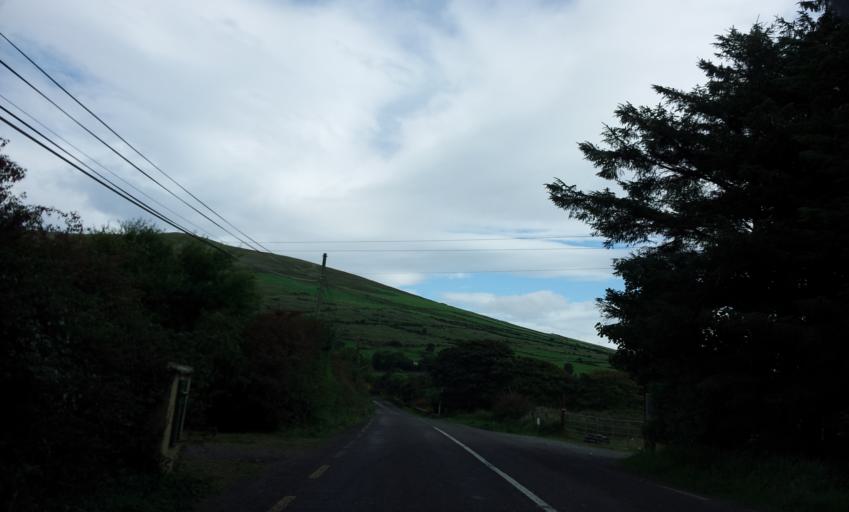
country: IE
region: Munster
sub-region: Ciarrai
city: Killorglin
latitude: 52.1815
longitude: -9.9695
